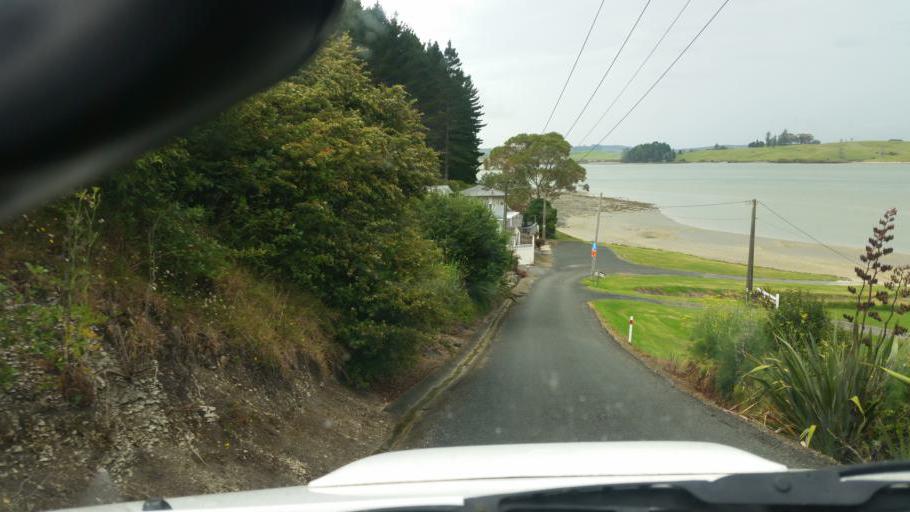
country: NZ
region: Auckland
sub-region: Auckland
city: Wellsford
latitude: -36.1560
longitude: 174.2236
